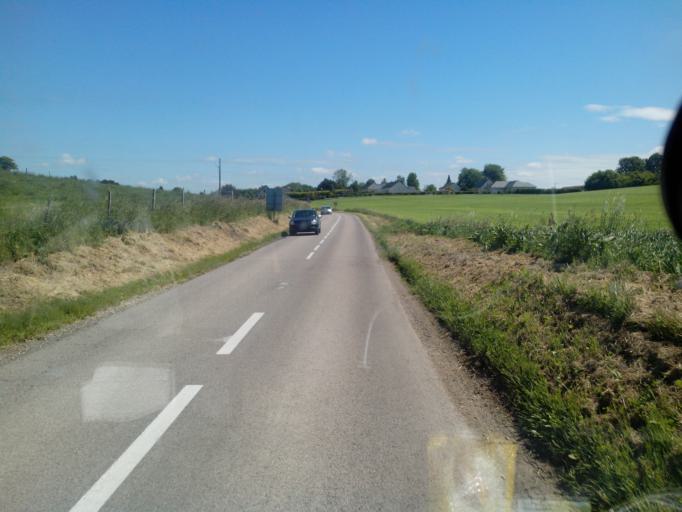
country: FR
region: Haute-Normandie
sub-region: Departement de la Seine-Maritime
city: Gonneville-la-Mallet
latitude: 49.6660
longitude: 0.1965
